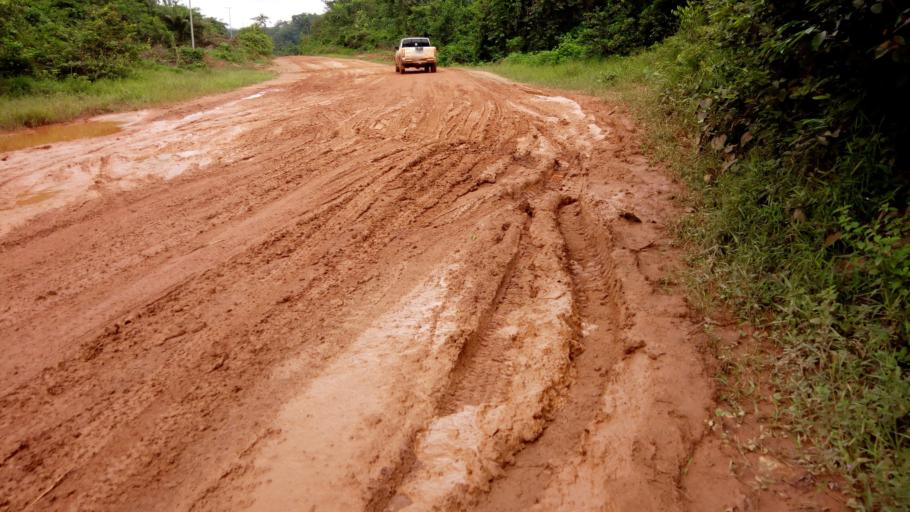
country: CI
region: Dix-Huit Montagnes
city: Toulepleu Guere
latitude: 6.3114
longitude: -8.5552
